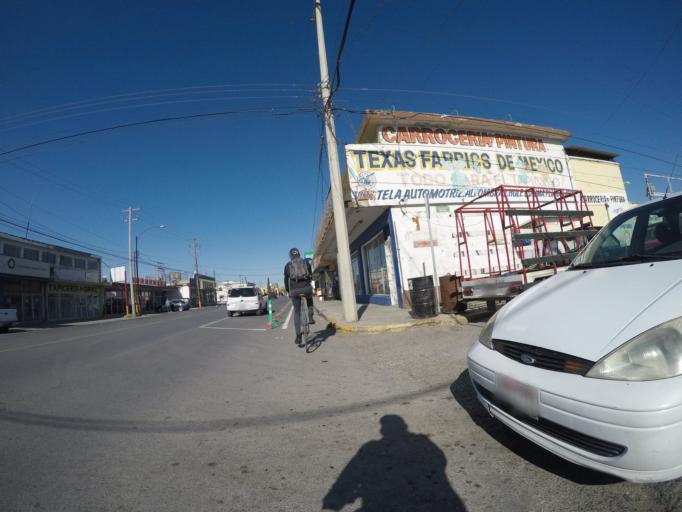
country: MX
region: Chihuahua
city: Ciudad Juarez
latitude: 31.7332
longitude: -106.4680
